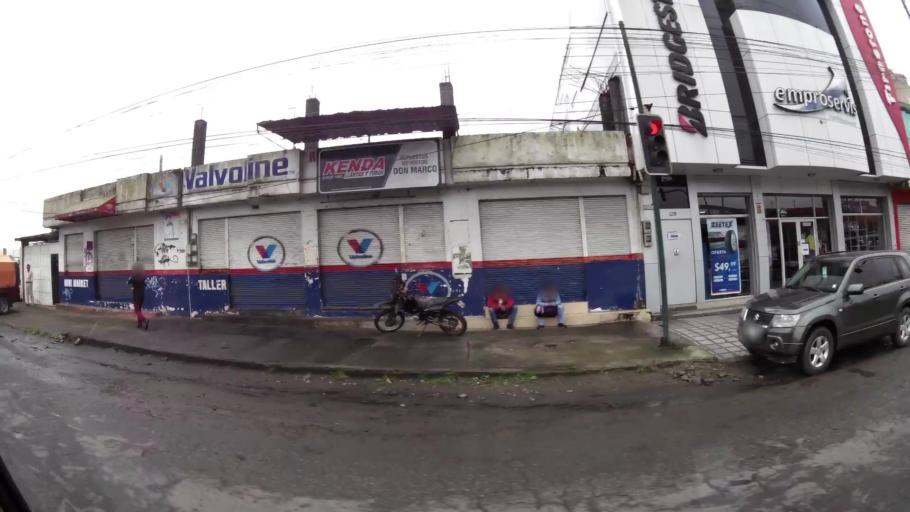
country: EC
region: Santo Domingo de los Tsachilas
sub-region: Canton Santo Domingo de los Colorados
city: Santo Domingo de los Colorados
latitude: -0.2634
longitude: -79.1891
